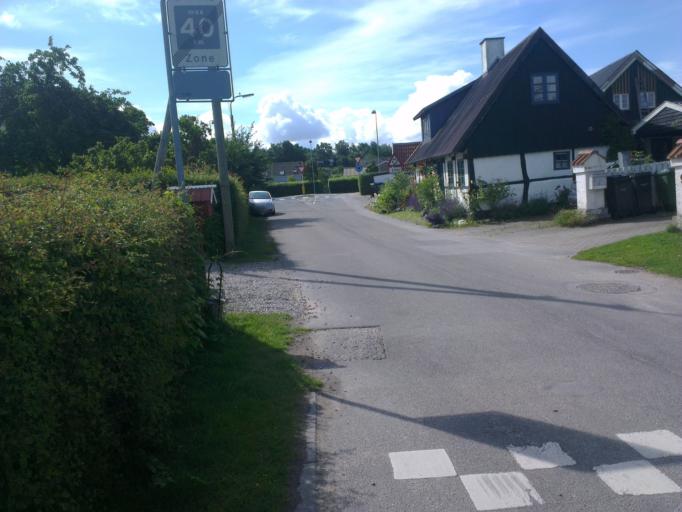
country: DK
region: Capital Region
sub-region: Frederikssund Kommune
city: Jaegerspris
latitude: 55.8560
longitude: 11.9986
